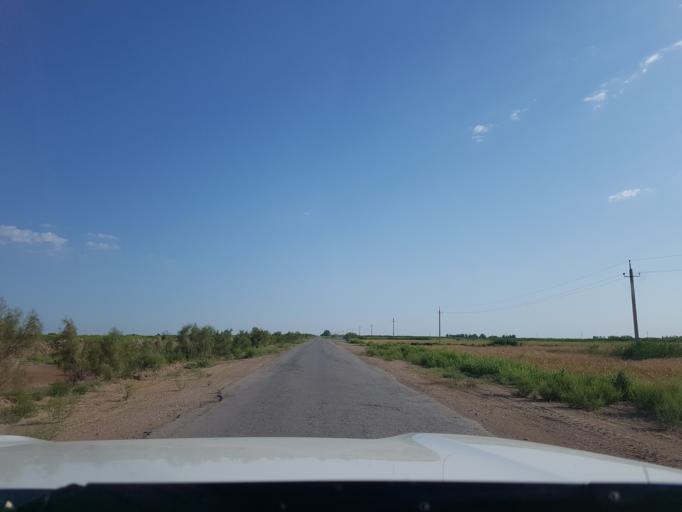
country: TM
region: Dasoguz
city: Koeneuergench
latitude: 41.9074
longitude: 58.7092
